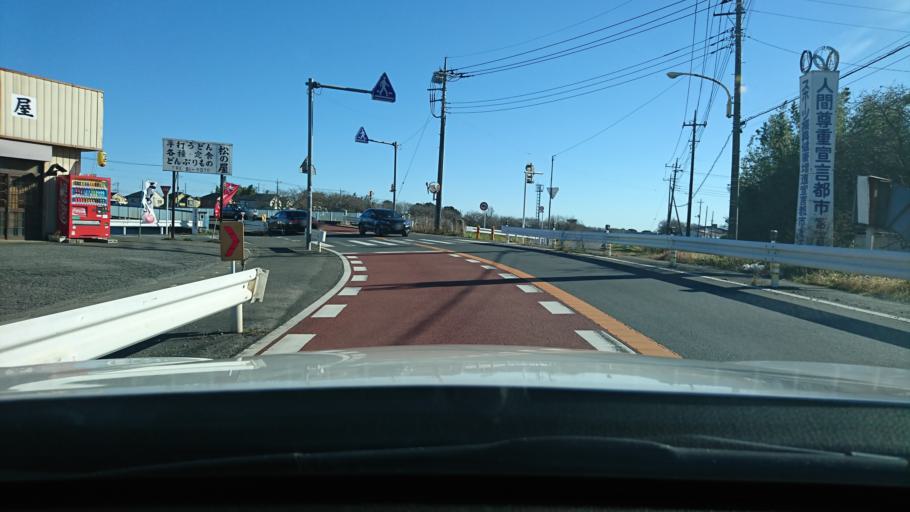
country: JP
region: Saitama
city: Kamifukuoka
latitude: 35.8827
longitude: 139.5518
